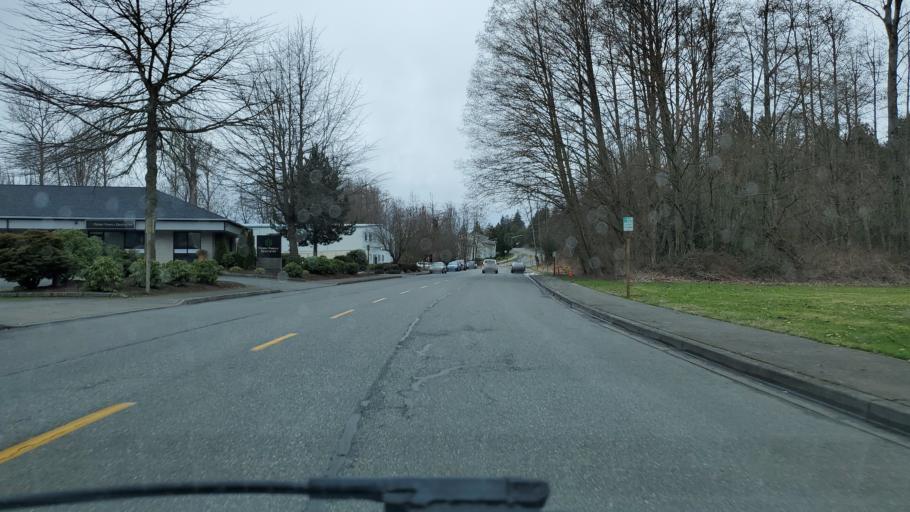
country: US
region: Washington
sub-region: Skagit County
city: Mount Vernon
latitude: 48.4388
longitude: -122.3257
